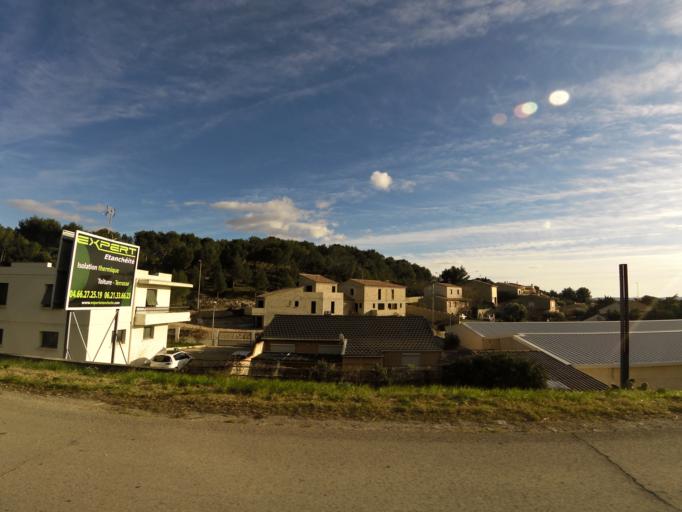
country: FR
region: Languedoc-Roussillon
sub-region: Departement du Gard
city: Nimes
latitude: 43.8219
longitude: 4.3253
